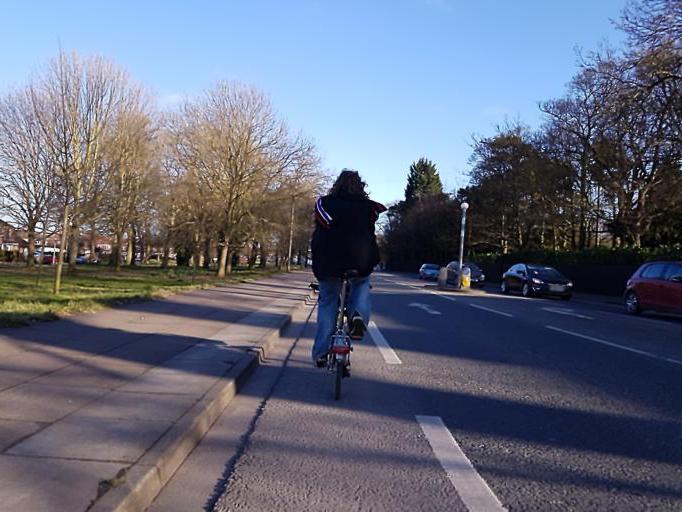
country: GB
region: England
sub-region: North East Lincolnshire
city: Grimsby
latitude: 53.5532
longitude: -0.0659
